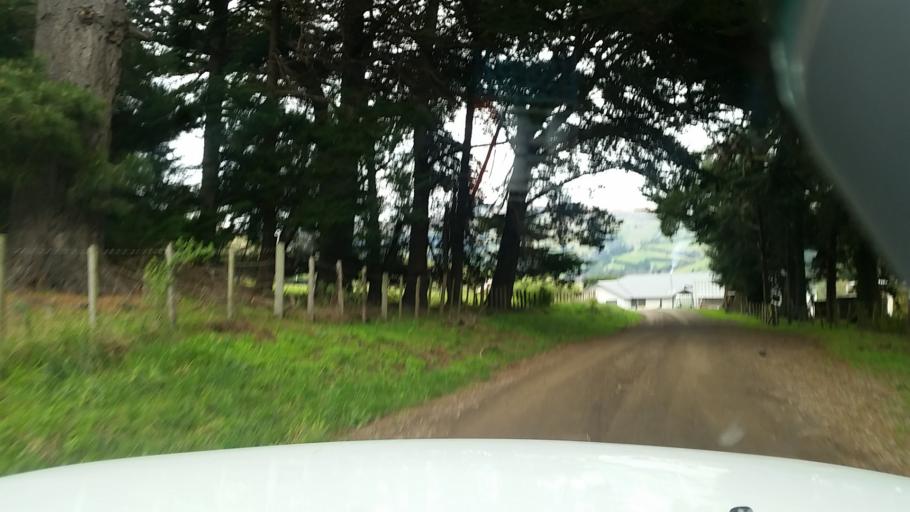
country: NZ
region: Canterbury
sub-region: Christchurch City
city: Christchurch
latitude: -43.6495
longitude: 172.8391
